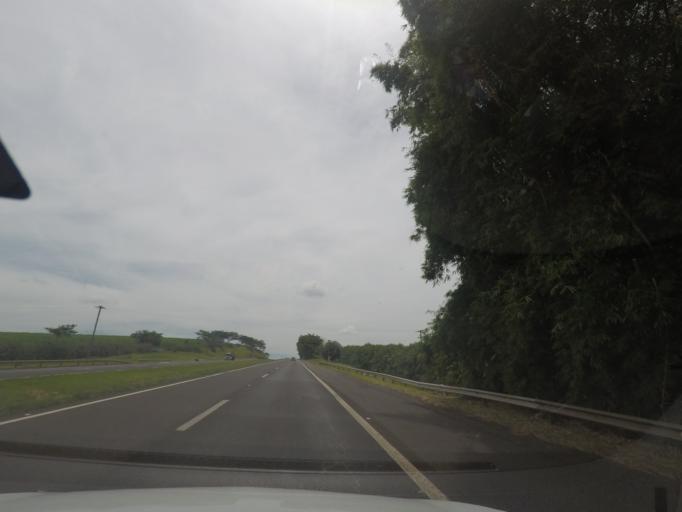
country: BR
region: Sao Paulo
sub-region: Bebedouro
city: Bebedouro
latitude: -21.0268
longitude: -48.4219
